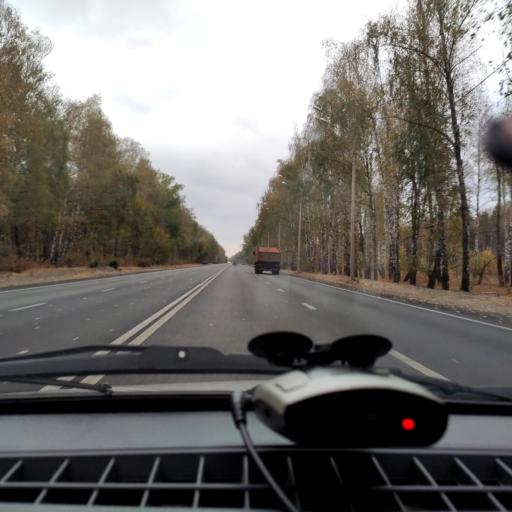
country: RU
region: Voronezj
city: Pridonskoy
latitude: 51.6943
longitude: 39.0917
